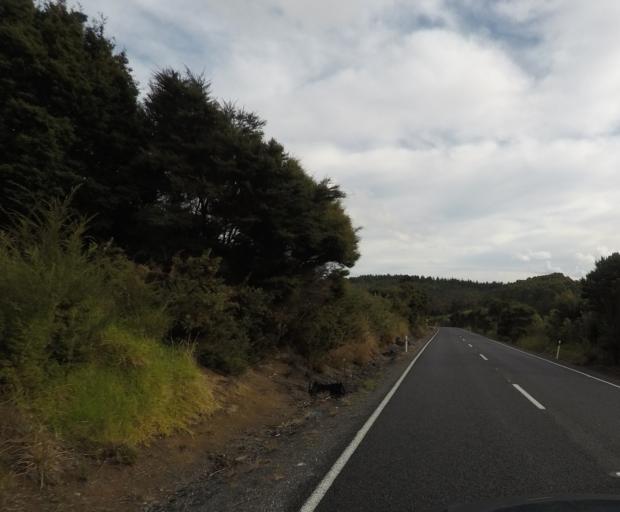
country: NZ
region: Northland
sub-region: Whangarei
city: Ruakaka
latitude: -36.0577
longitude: 174.5591
